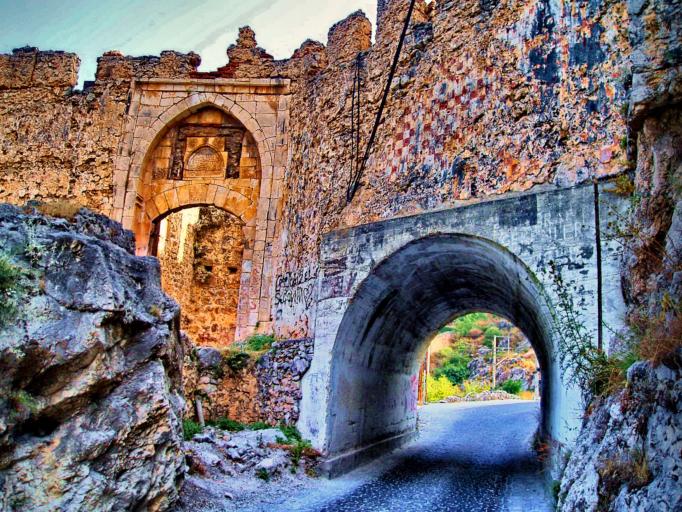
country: TR
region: Antalya
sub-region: Alanya
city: Alanya
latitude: 36.5360
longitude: 31.9939
